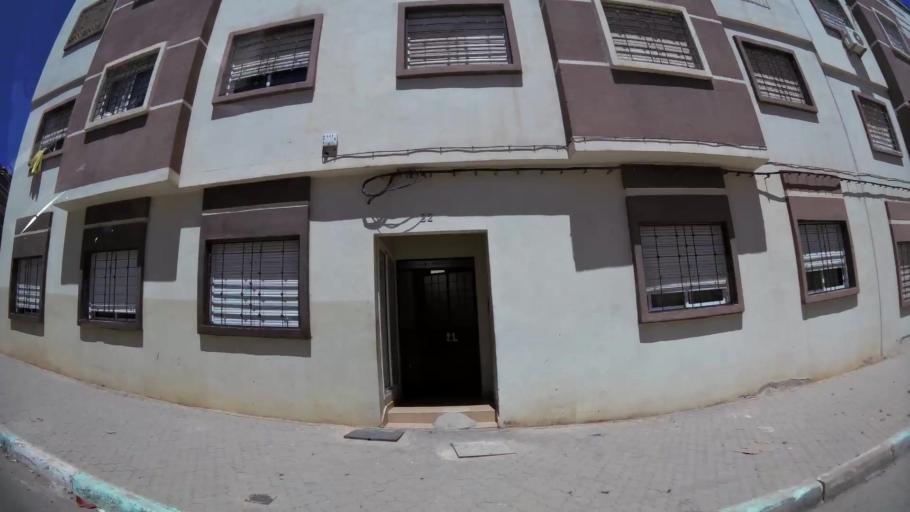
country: MA
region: Oriental
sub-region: Oujda-Angad
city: Oujda
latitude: 34.6554
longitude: -1.9454
